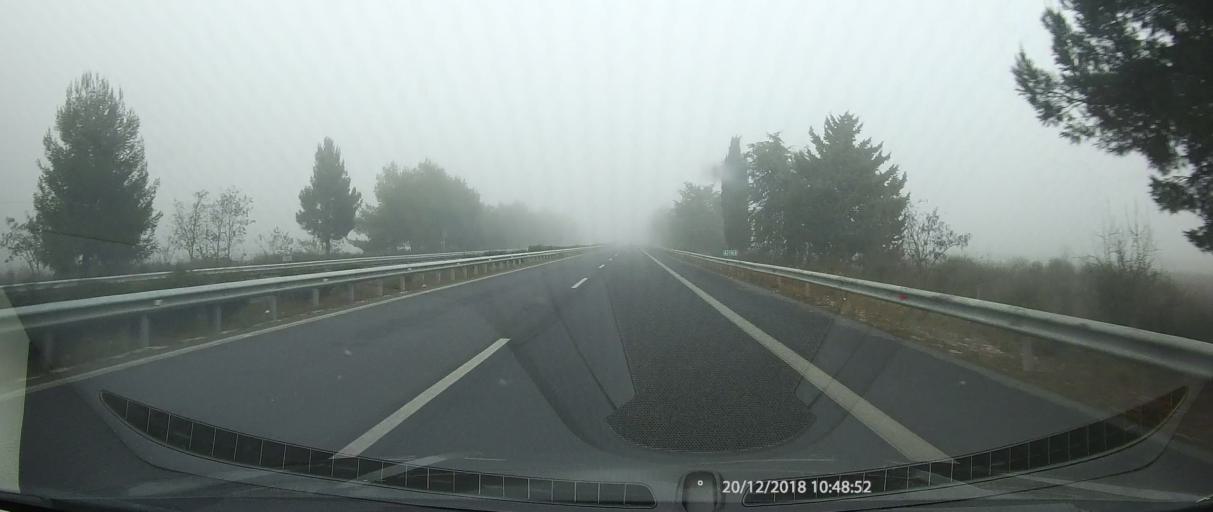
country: GR
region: Peloponnese
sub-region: Nomos Arkadias
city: Tripoli
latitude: 37.5262
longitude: 22.4098
